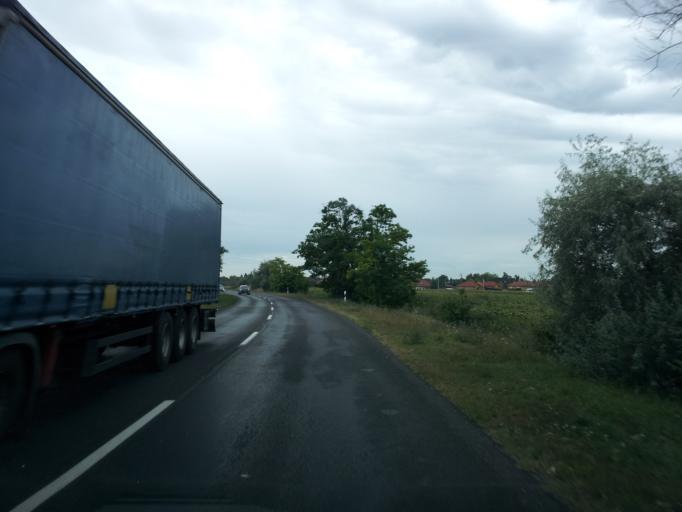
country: HU
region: Fejer
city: Kapolnasnyek
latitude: 47.2465
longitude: 18.6659
